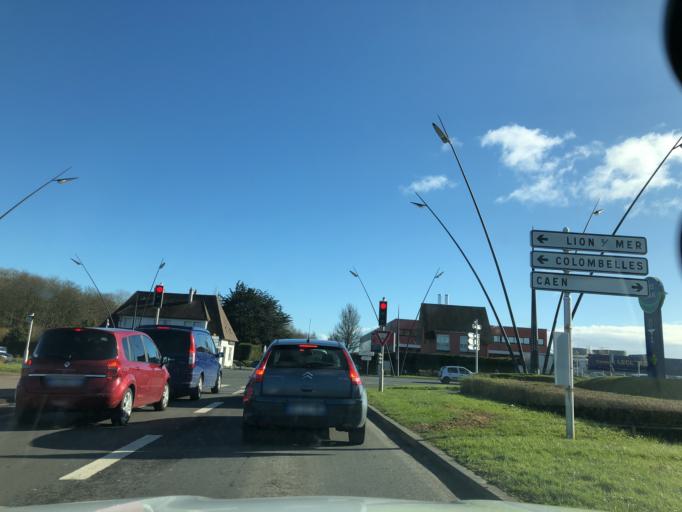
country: FR
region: Lower Normandy
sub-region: Departement du Calvados
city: Epron
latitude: 49.2128
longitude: -0.3426
